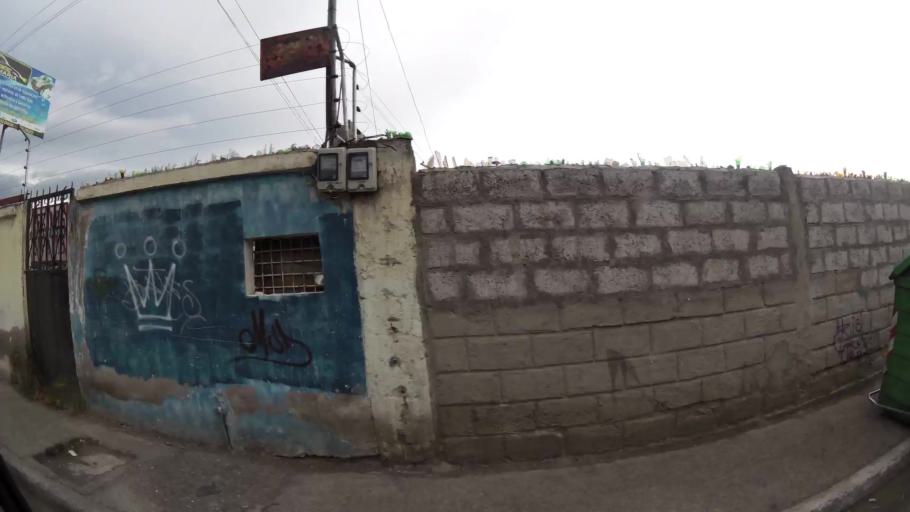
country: EC
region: Tungurahua
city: Ambato
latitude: -1.2730
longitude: -78.6280
